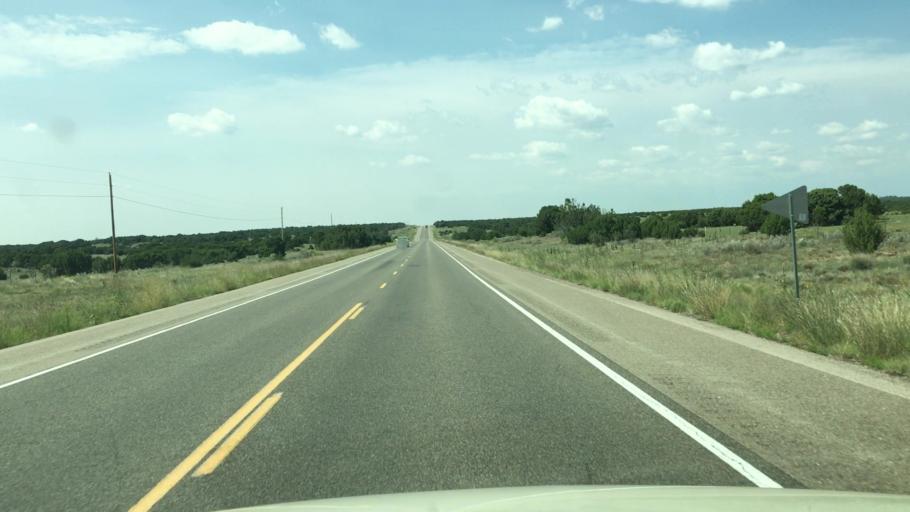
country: US
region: New Mexico
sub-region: Torrance County
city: Moriarty
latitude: 35.0482
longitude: -105.6865
